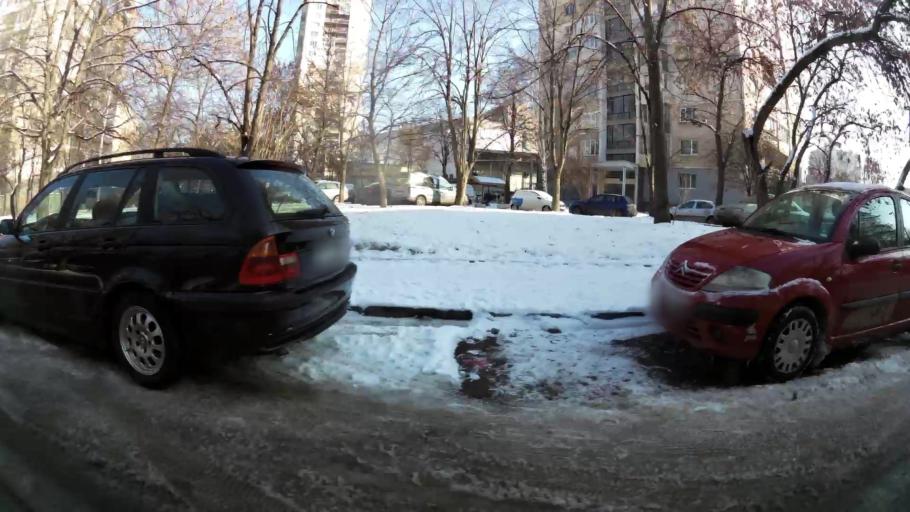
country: BG
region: Sofia-Capital
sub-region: Stolichna Obshtina
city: Sofia
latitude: 42.6588
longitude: 23.3399
